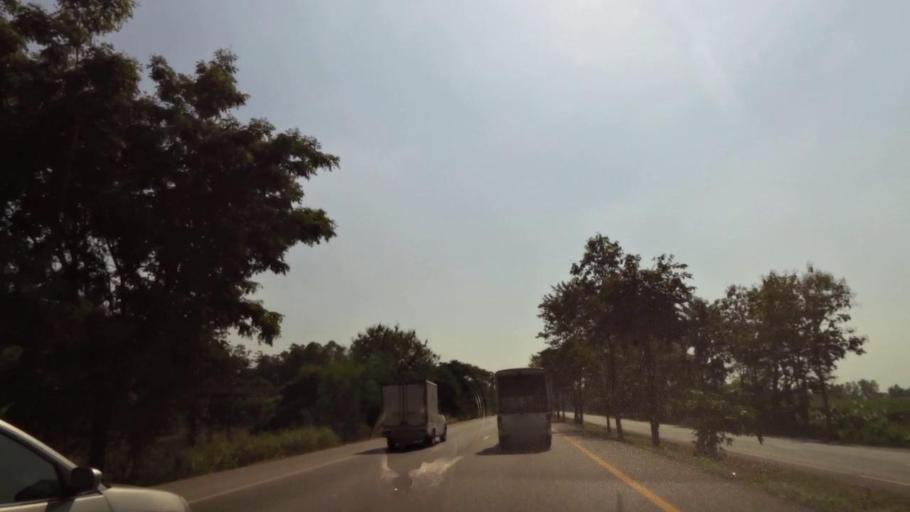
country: TH
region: Phichit
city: Bueng Na Rang
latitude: 16.1082
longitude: 100.1258
